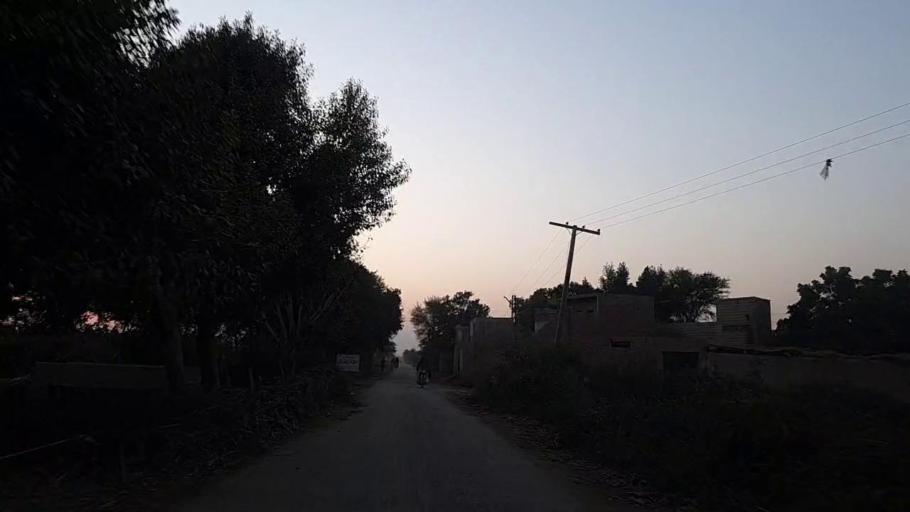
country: PK
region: Sindh
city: Hala
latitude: 25.9597
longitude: 68.4009
